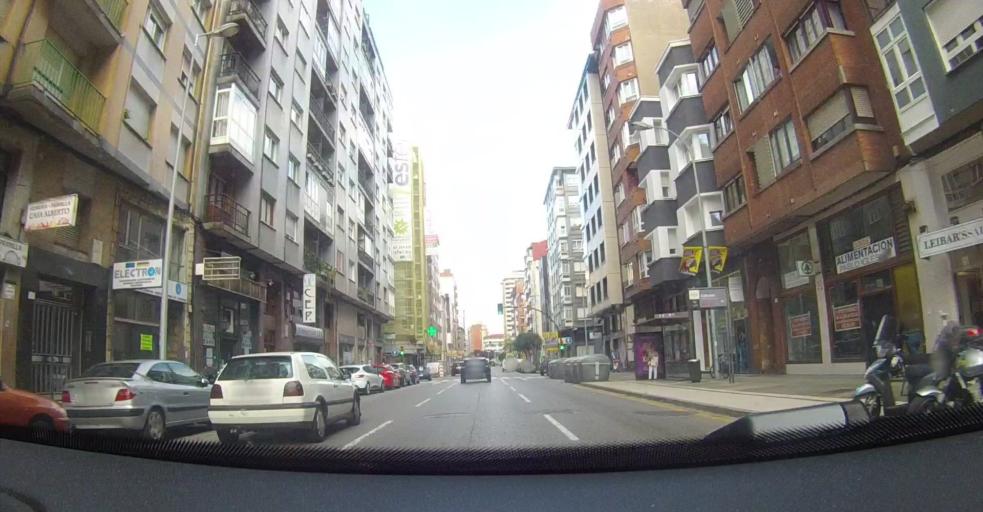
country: ES
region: Asturias
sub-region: Province of Asturias
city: Gijon
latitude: 43.5360
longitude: -5.6571
